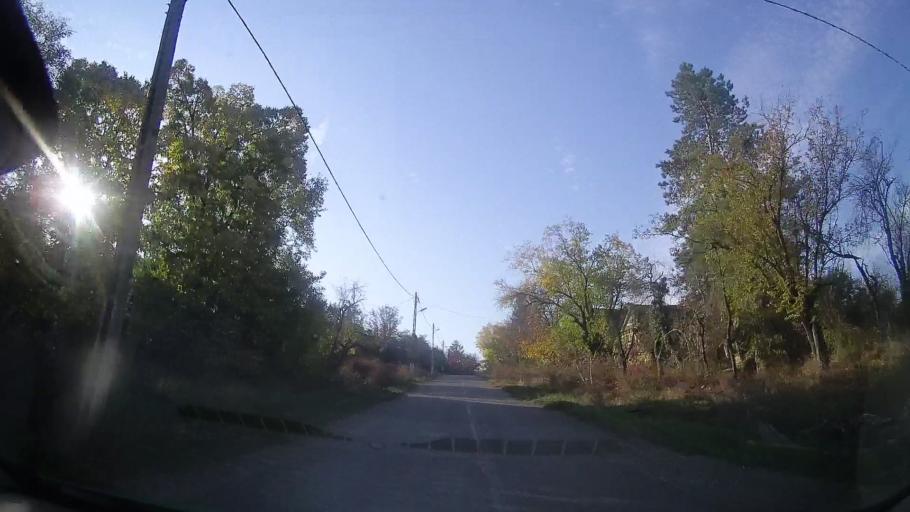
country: RO
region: Timis
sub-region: Comuna Bogda
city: Bogda
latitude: 45.9584
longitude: 21.6148
